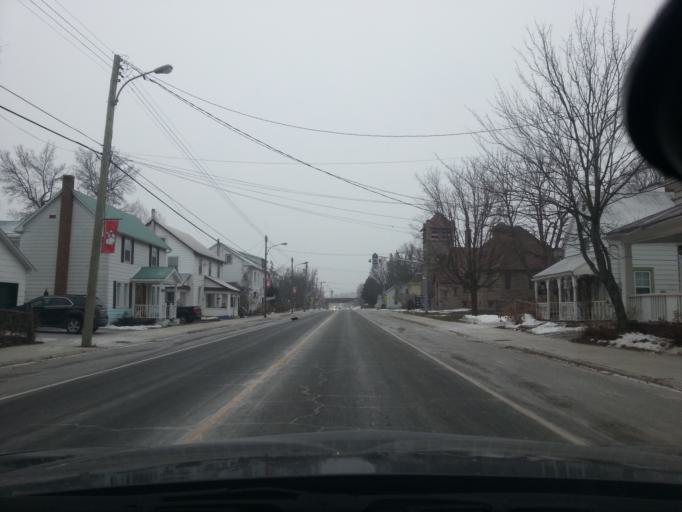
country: CA
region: Ontario
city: Arnprior
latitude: 45.3319
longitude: -76.2907
